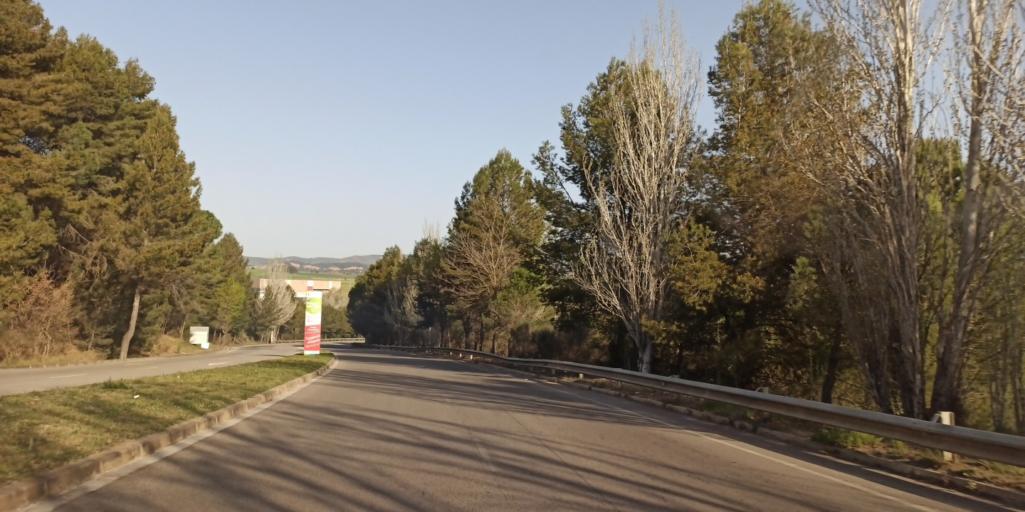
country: ES
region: Catalonia
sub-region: Provincia de Barcelona
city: La Pobla de Claramunt
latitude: 41.5735
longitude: 1.6669
